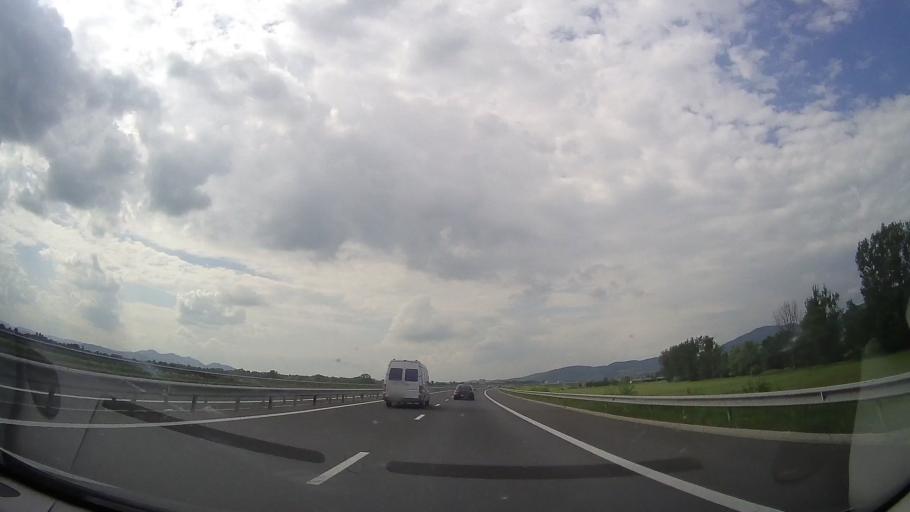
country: RO
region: Hunedoara
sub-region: Oras Simeria
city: Simeria
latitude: 45.8550
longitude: 23.0325
